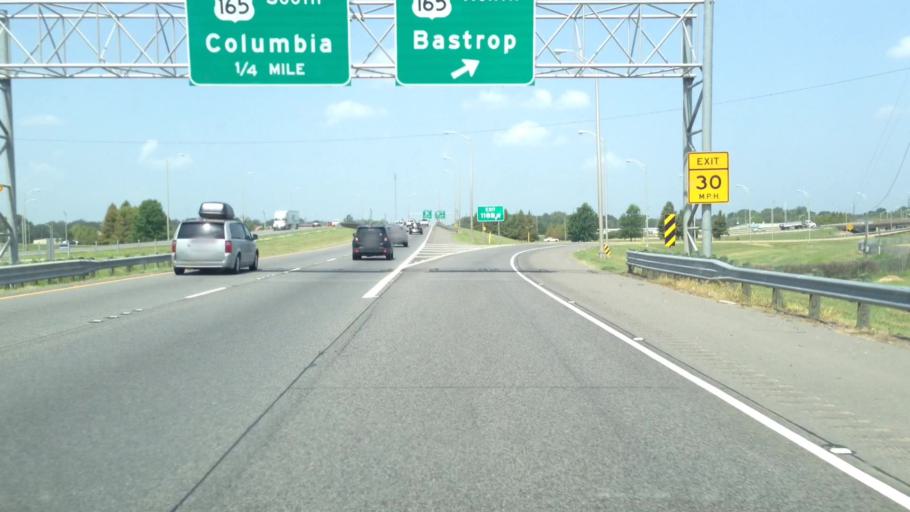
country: US
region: Louisiana
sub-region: Ouachita Parish
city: Monroe
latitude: 32.4992
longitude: -92.0789
